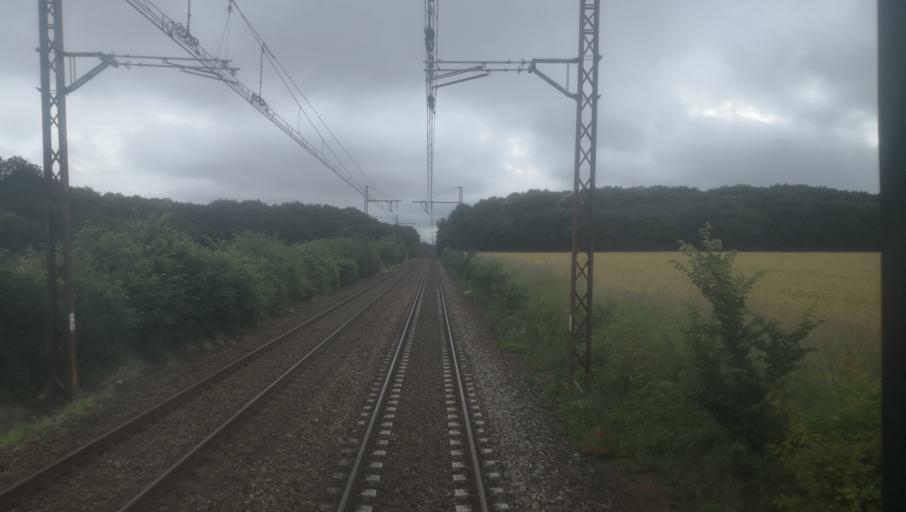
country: FR
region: Centre
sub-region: Departement de l'Indre
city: Montierchaume
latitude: 46.8326
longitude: 1.7537
